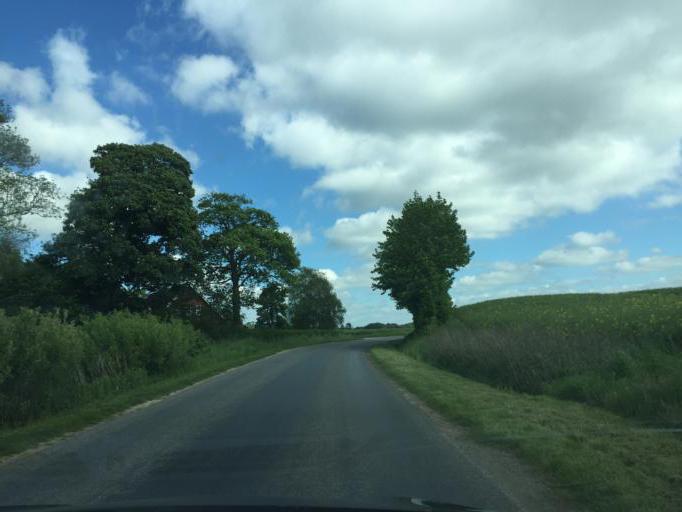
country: DK
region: South Denmark
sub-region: Assens Kommune
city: Tommerup
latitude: 55.3429
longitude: 10.2249
